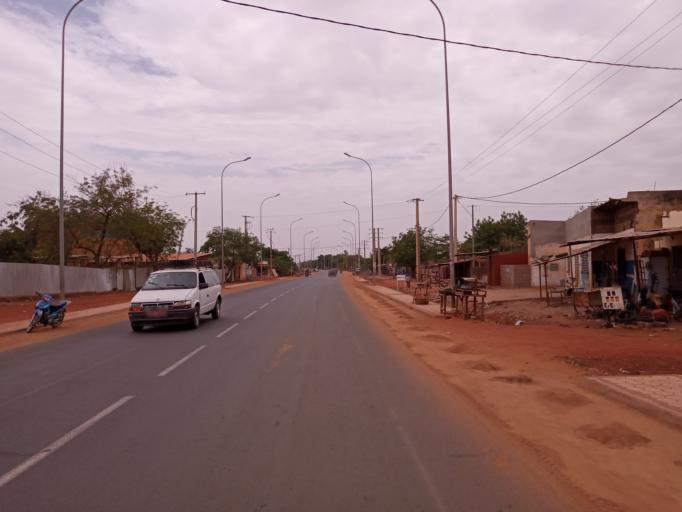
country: ML
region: Koulikoro
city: Koulikoro
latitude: 12.8529
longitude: -7.5680
